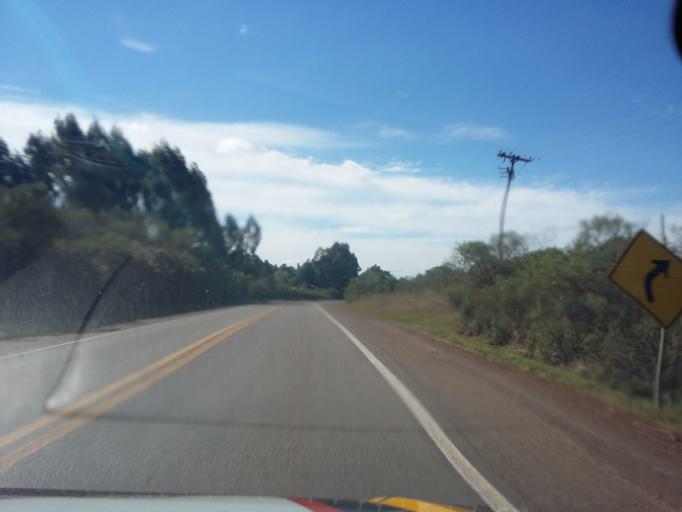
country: BR
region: Rio Grande do Sul
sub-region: Vacaria
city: Vacaria
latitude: -28.7034
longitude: -51.0781
